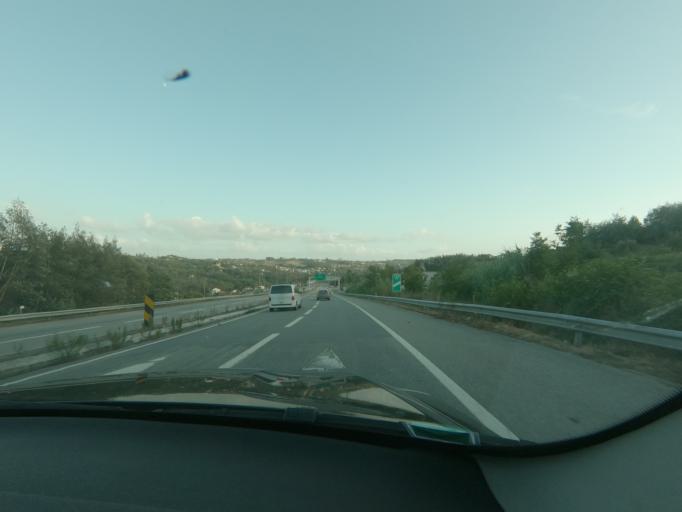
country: PT
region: Viseu
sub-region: Santa Comba Dao
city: Santa Comba Dao
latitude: 40.4029
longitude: -8.1263
